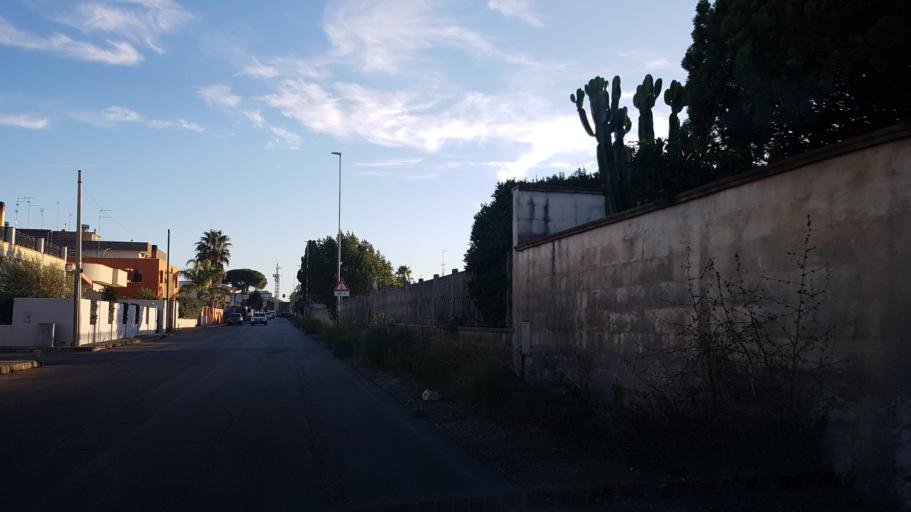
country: IT
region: Apulia
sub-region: Provincia di Lecce
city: Lecce
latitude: 40.3730
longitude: 18.1793
